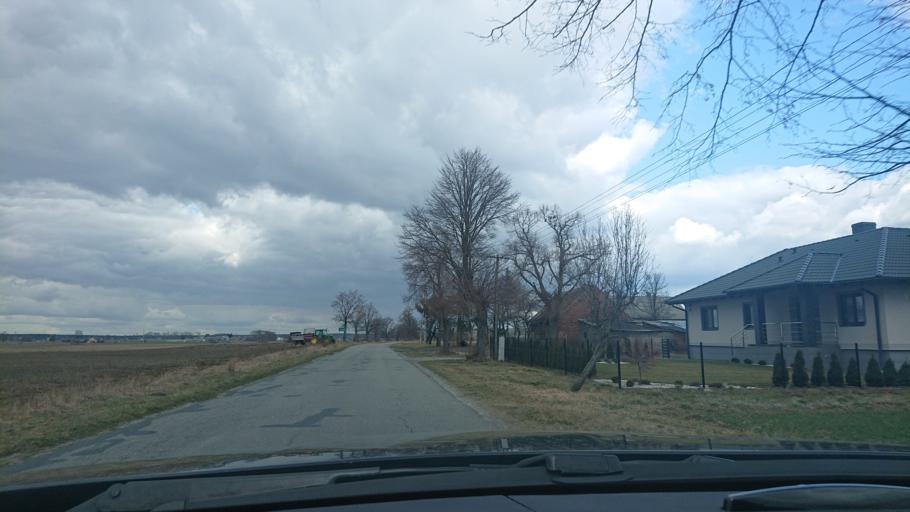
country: PL
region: Greater Poland Voivodeship
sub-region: Powiat gnieznienski
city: Niechanowo
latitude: 52.5658
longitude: 17.7008
